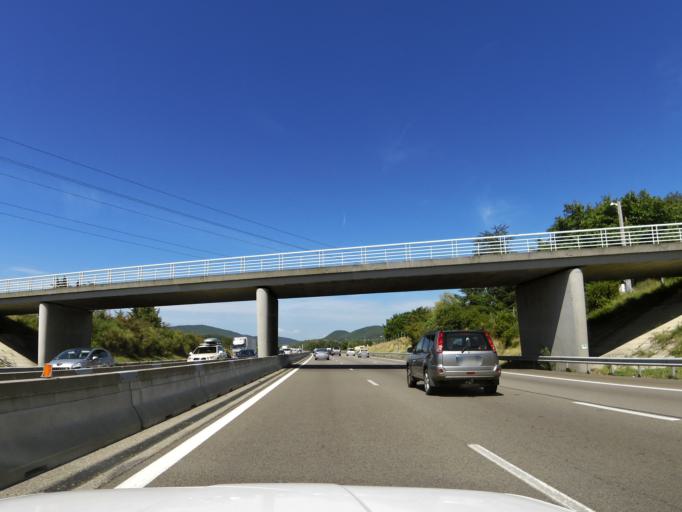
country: FR
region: Rhone-Alpes
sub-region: Departement de la Drome
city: Montboucher-sur-Jabron
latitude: 44.5707
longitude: 4.8092
